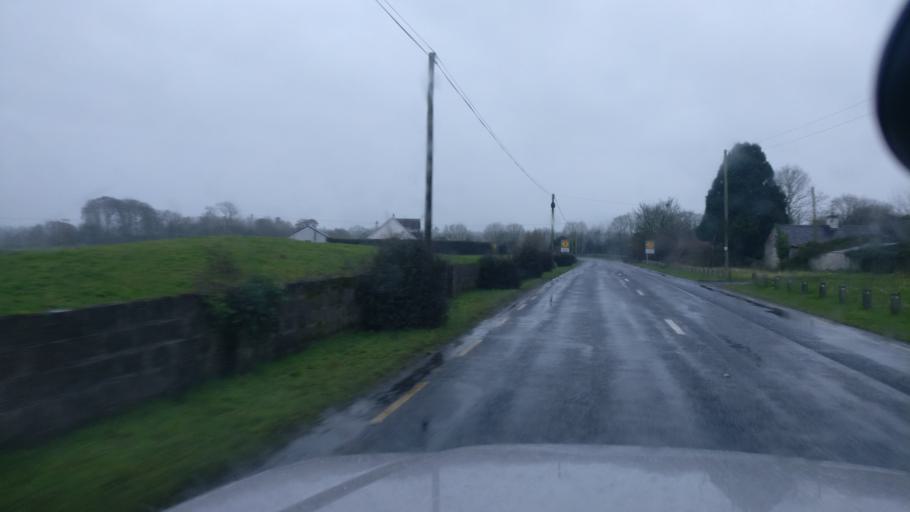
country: IE
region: Connaught
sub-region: County Galway
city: Portumna
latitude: 53.1479
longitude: -8.1959
